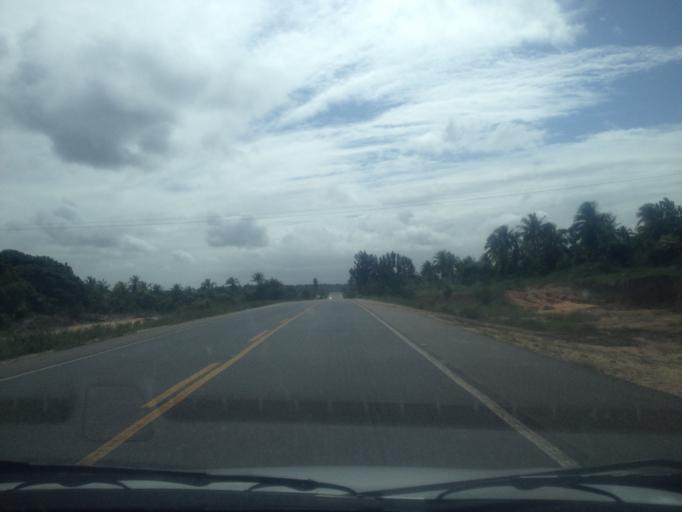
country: BR
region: Bahia
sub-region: Conde
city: Conde
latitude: -11.8578
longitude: -37.6326
